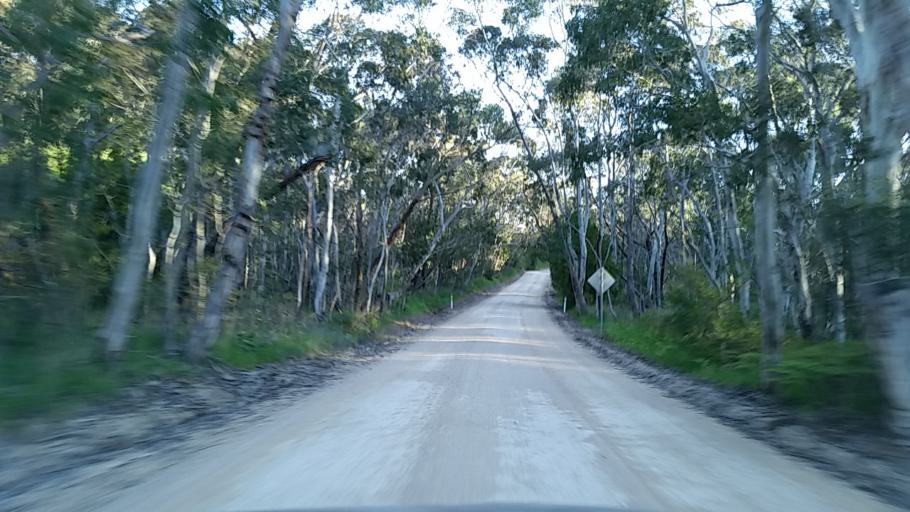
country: AU
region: South Australia
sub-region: Alexandrina
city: Mount Compass
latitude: -35.2742
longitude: 138.7014
